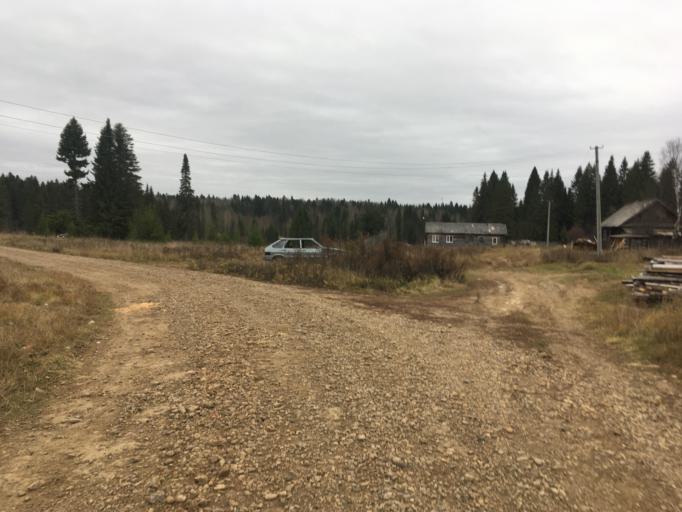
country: RU
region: Perm
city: Komarikhinskiy
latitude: 58.0885
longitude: 57.1089
